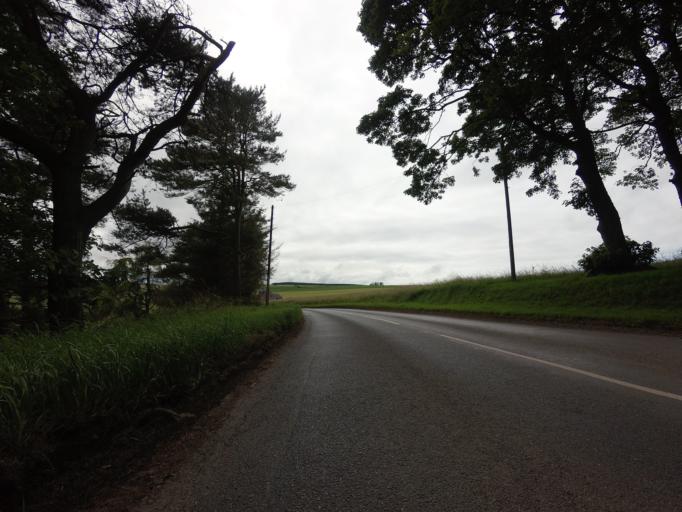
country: GB
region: Scotland
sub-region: Aberdeenshire
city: Turriff
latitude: 57.5443
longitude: -2.3566
